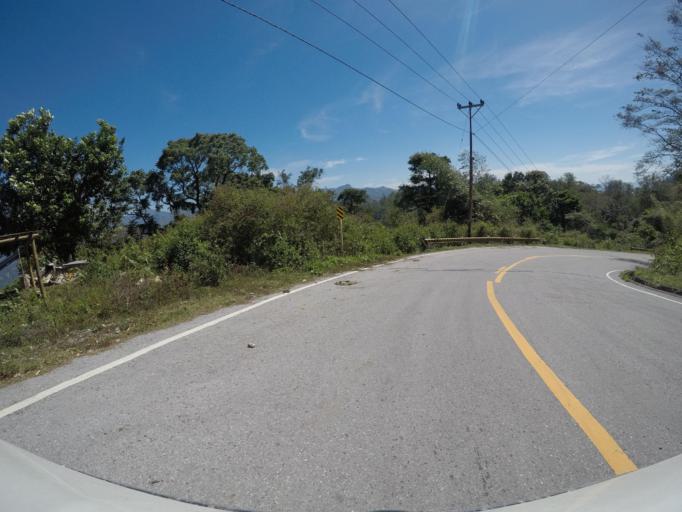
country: TL
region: Manufahi
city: Same
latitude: -8.8976
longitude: 125.9804
